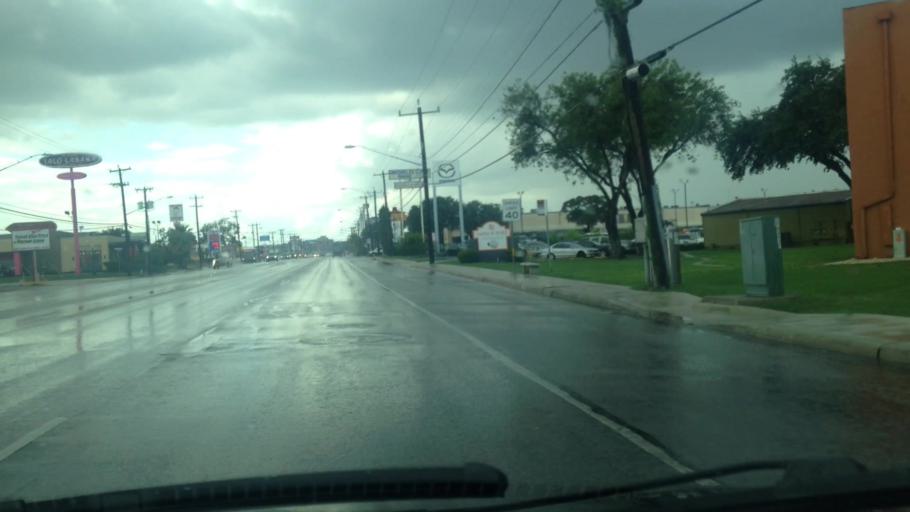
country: US
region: Texas
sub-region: Bexar County
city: Balcones Heights
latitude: 29.4852
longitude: -98.5465
